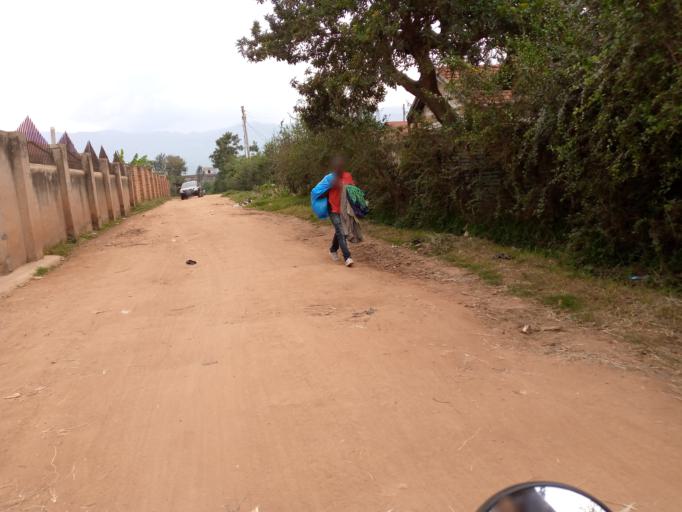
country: UG
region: Eastern Region
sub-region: Mbale District
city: Mbale
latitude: 1.0851
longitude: 34.1693
